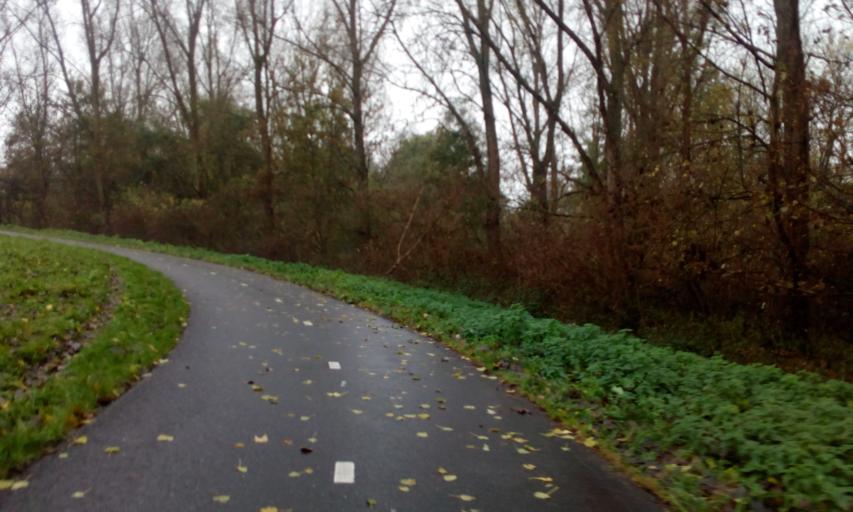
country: NL
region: South Holland
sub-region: Gemeente Lansingerland
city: Bleiswijk
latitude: 51.9939
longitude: 4.5462
